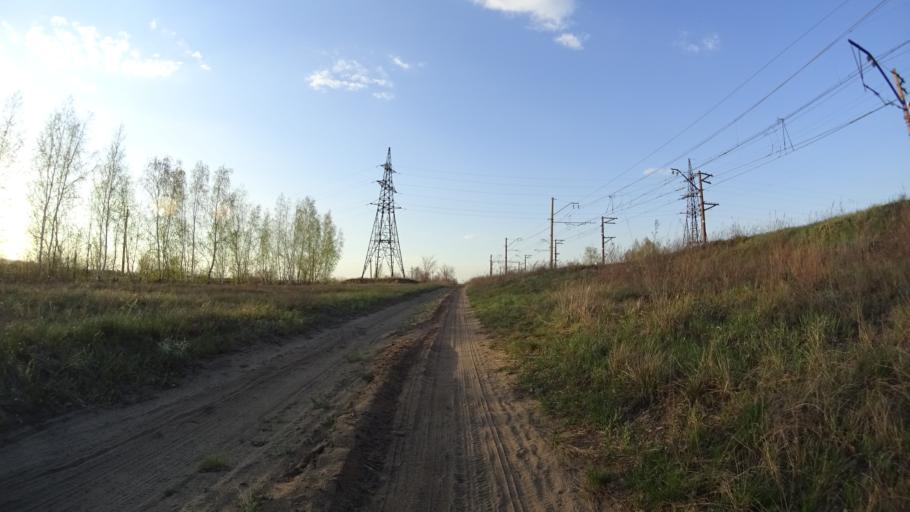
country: RU
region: Chelyabinsk
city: Troitsk
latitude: 54.0603
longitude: 61.6136
